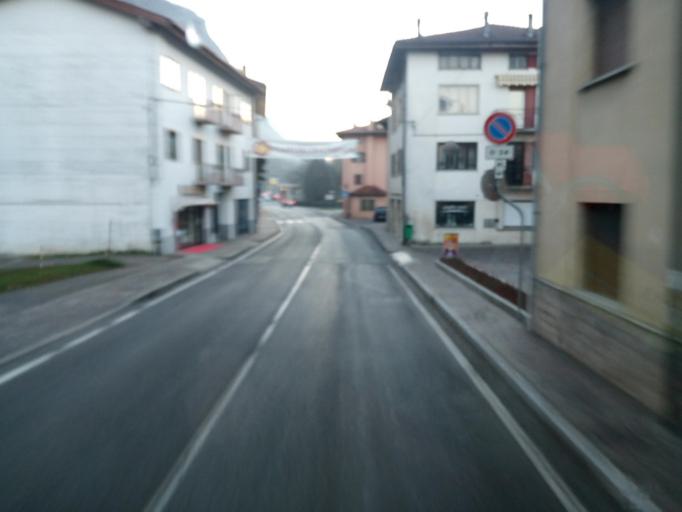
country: IT
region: Friuli Venezia Giulia
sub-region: Provincia di Udine
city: Villa Santina
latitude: 46.4158
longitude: 12.9253
